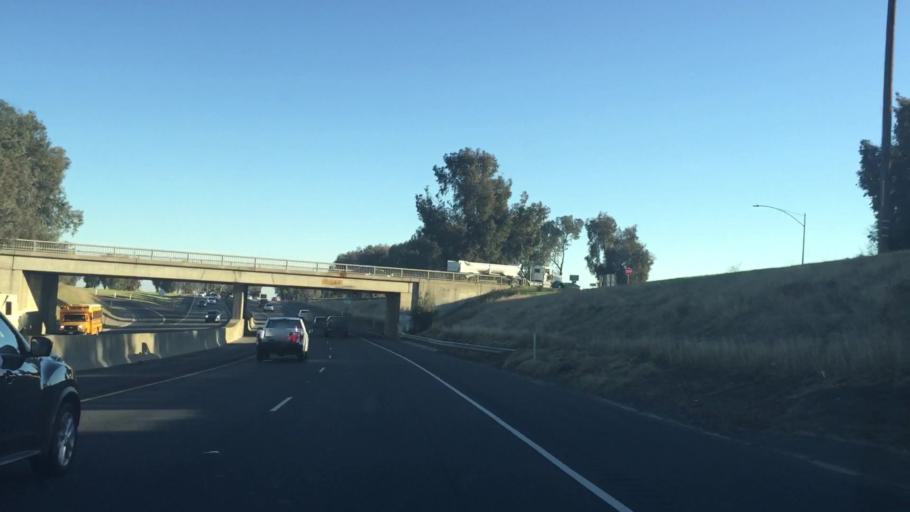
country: US
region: California
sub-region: Yuba County
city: Olivehurst
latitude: 39.1030
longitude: -121.5513
